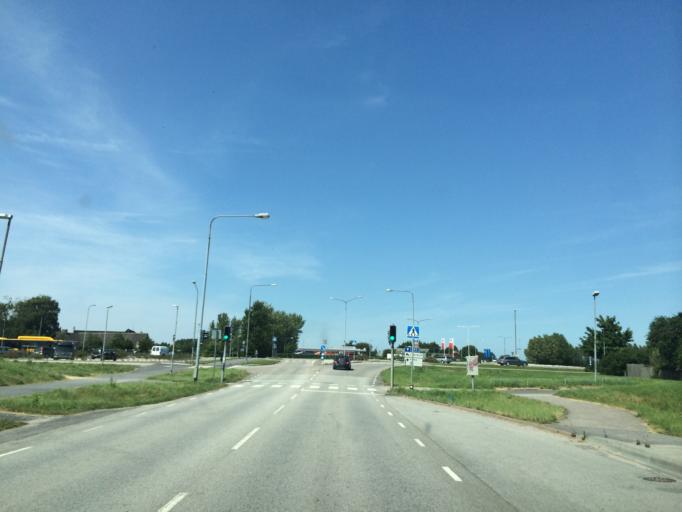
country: SE
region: Skane
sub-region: Vellinge Kommun
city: Hollviken
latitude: 55.4233
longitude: 12.9617
